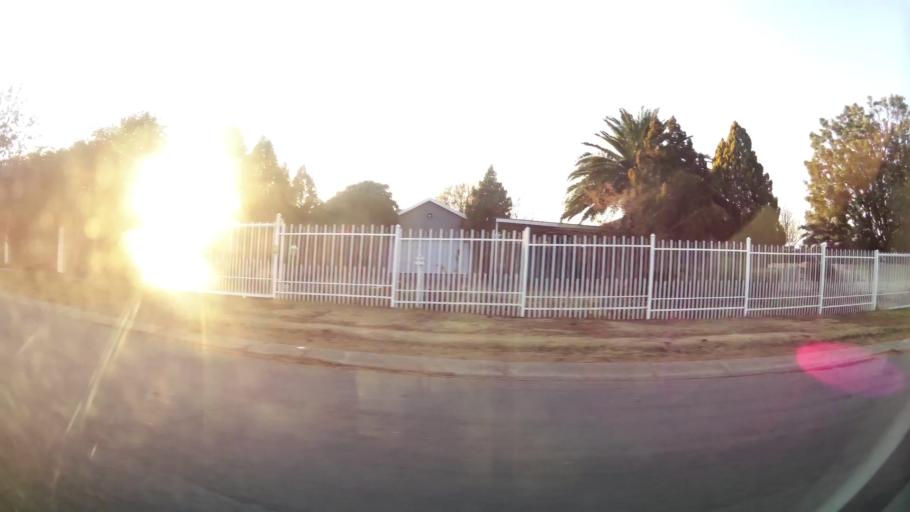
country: ZA
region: Orange Free State
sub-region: Mangaung Metropolitan Municipality
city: Bloemfontein
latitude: -29.0987
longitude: 26.1604
